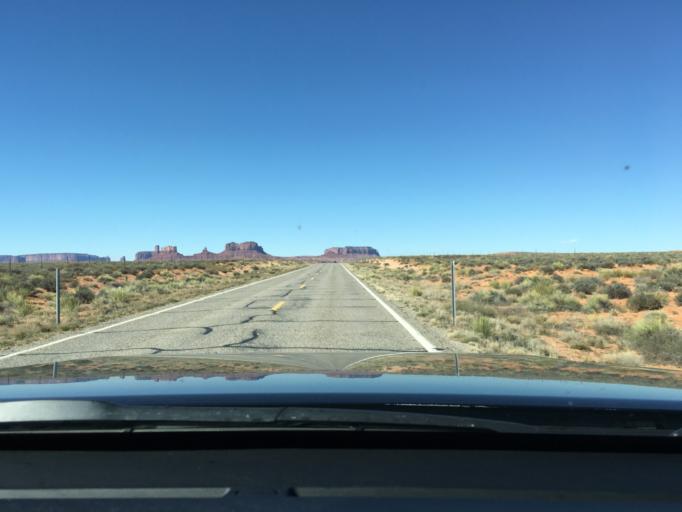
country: US
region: Arizona
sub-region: Navajo County
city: Kayenta
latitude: 37.1080
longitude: -109.9783
